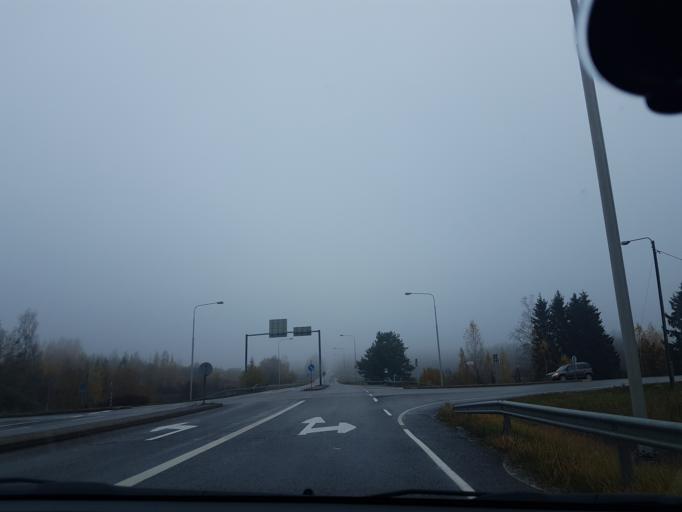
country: FI
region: Uusimaa
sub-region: Helsinki
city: Jaervenpaeae
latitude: 60.4698
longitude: 25.1416
